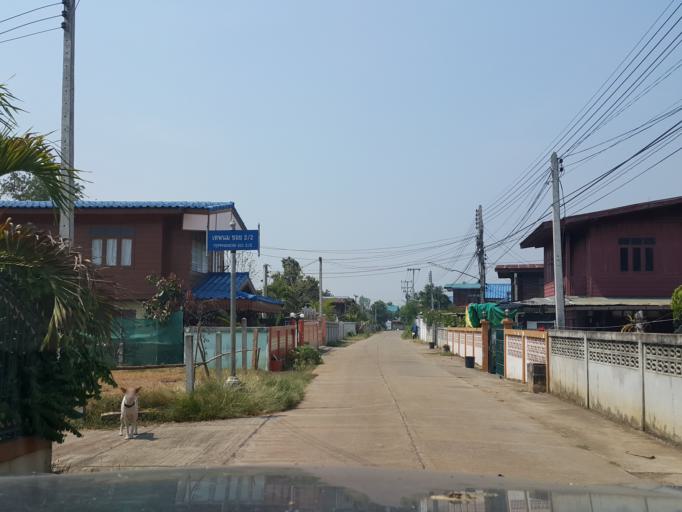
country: TH
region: Sukhothai
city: Thung Saliam
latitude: 17.3150
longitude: 99.5458
